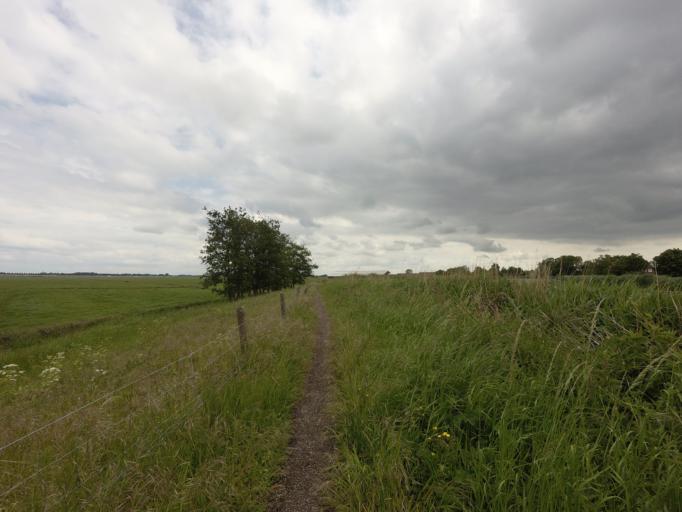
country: NL
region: North Holland
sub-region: Gemeente Ouder-Amstel
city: Ouderkerk aan de Amstel
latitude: 52.2774
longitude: 4.9267
